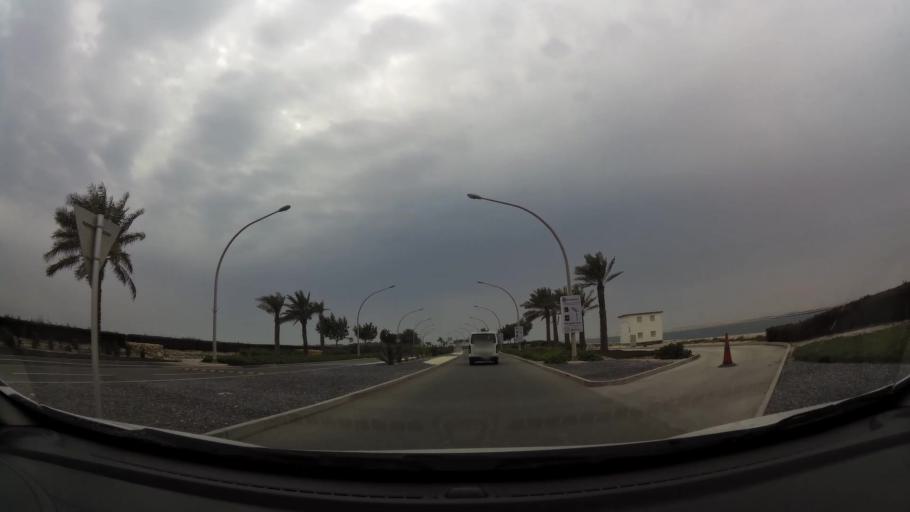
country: BH
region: Central Governorate
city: Dar Kulayb
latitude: 25.8485
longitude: 50.6057
